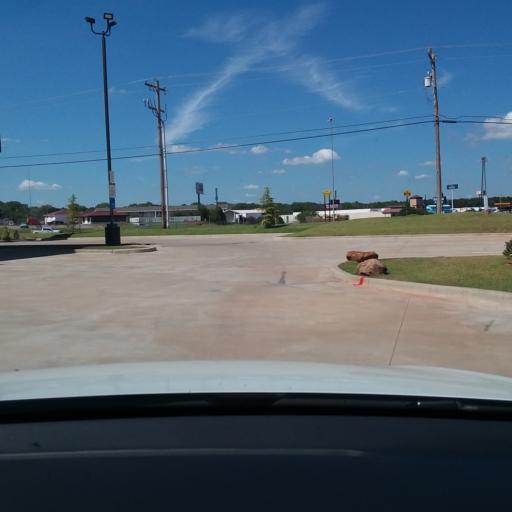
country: US
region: Oklahoma
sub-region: Oklahoma County
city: Edmond
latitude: 35.5906
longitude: -97.4336
